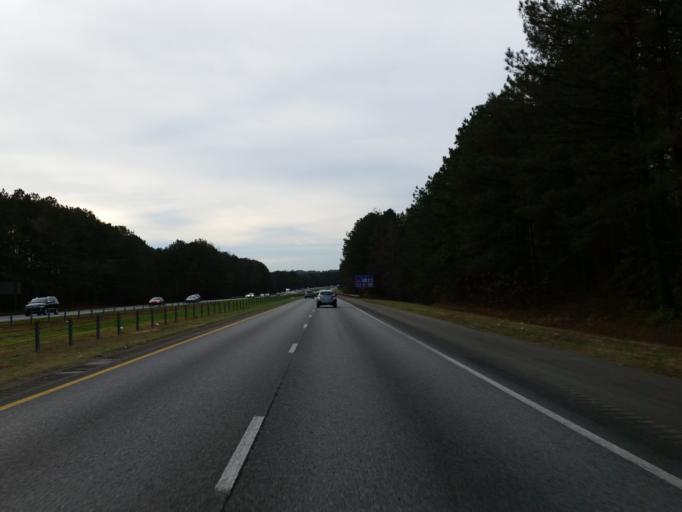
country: US
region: Georgia
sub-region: Cherokee County
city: Holly Springs
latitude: 34.1686
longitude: -84.5129
